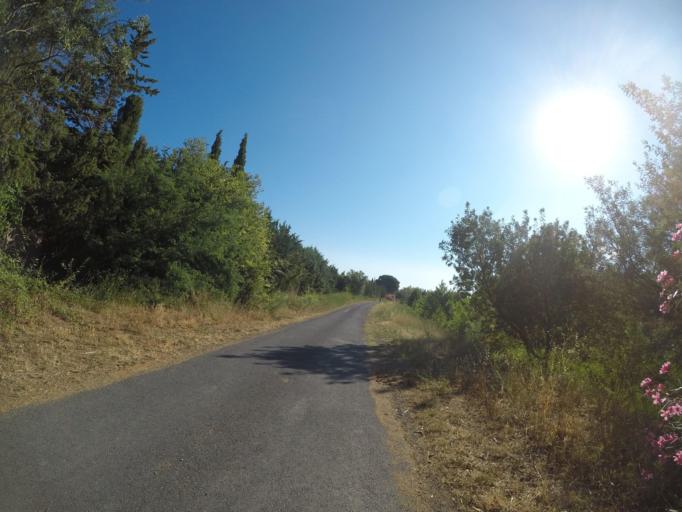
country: FR
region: Languedoc-Roussillon
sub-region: Departement des Pyrenees-Orientales
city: Pezilla-la-Riviere
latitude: 42.6771
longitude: 2.7690
